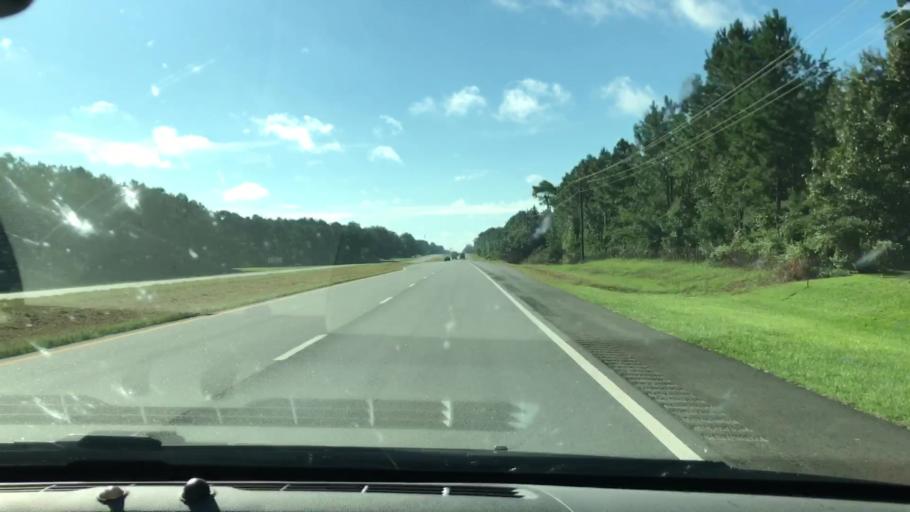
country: US
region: Georgia
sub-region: Lee County
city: Leesburg
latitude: 31.6747
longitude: -84.2931
